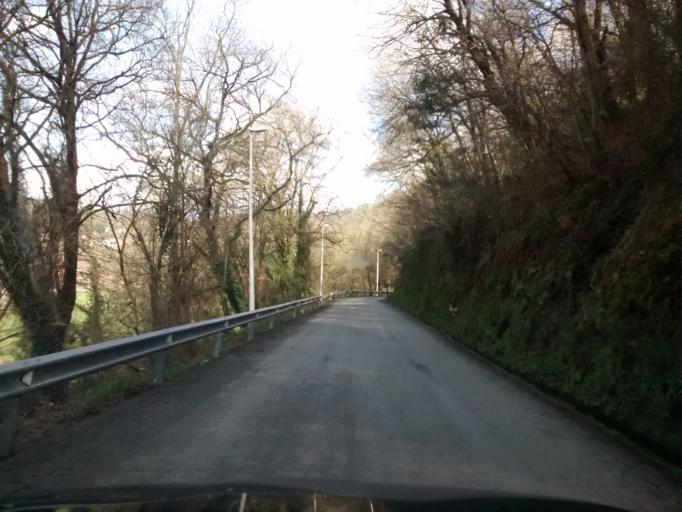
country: ES
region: Cantabria
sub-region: Provincia de Cantabria
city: Lierganes
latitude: 43.3457
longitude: -3.7143
